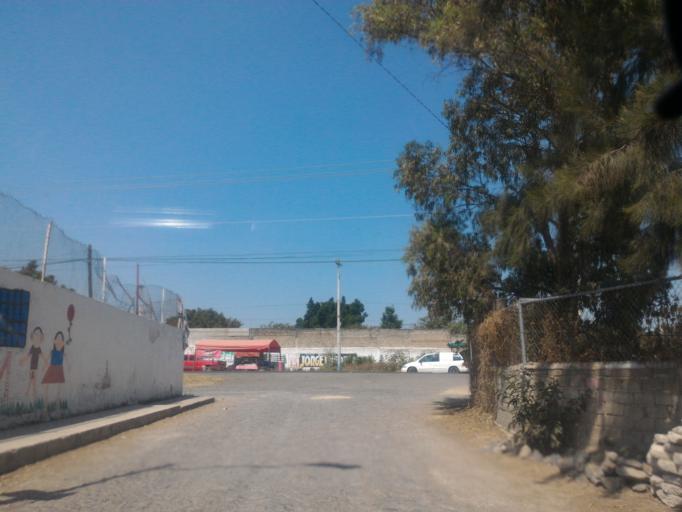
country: MX
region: Jalisco
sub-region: San Pedro Tlaquepaque
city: Paseo del Prado
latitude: 20.5661
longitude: -103.4102
